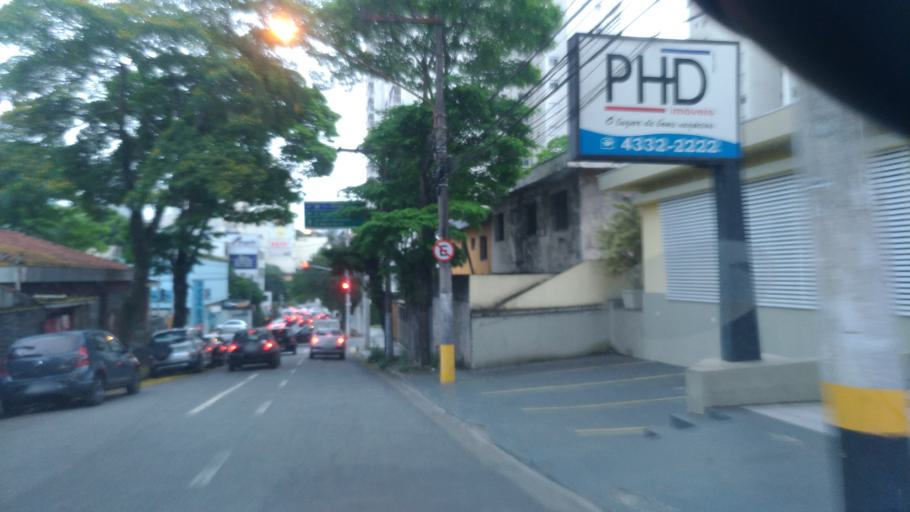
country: BR
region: Sao Paulo
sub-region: Sao Bernardo Do Campo
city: Sao Bernardo do Campo
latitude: -23.7035
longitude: -46.5445
